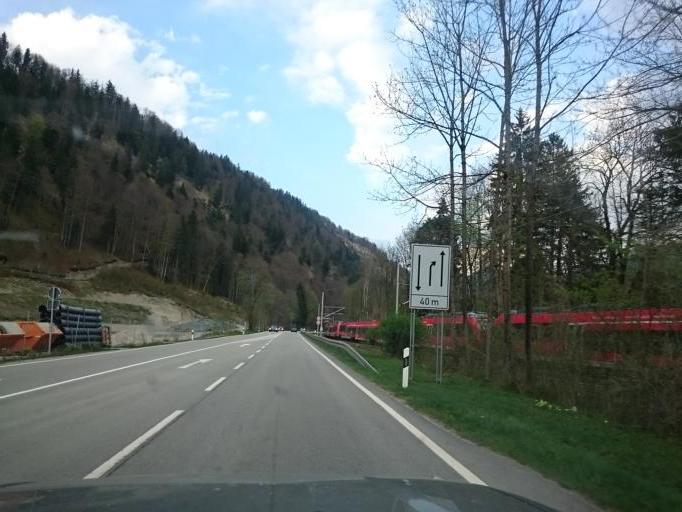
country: DE
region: Bavaria
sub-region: Upper Bavaria
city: Oberau
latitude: 47.5688
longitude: 11.1446
